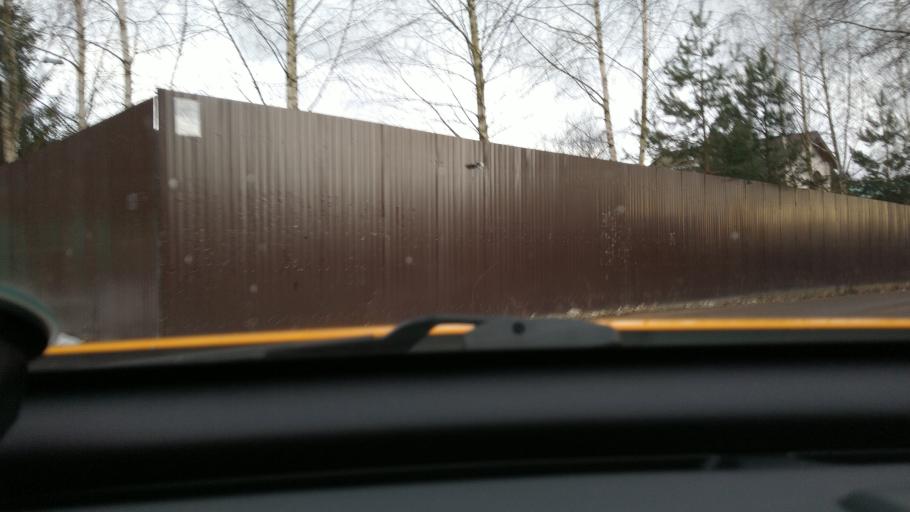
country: RU
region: Moskovskaya
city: Petrovo-Dal'neye
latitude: 55.7683
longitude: 37.2082
